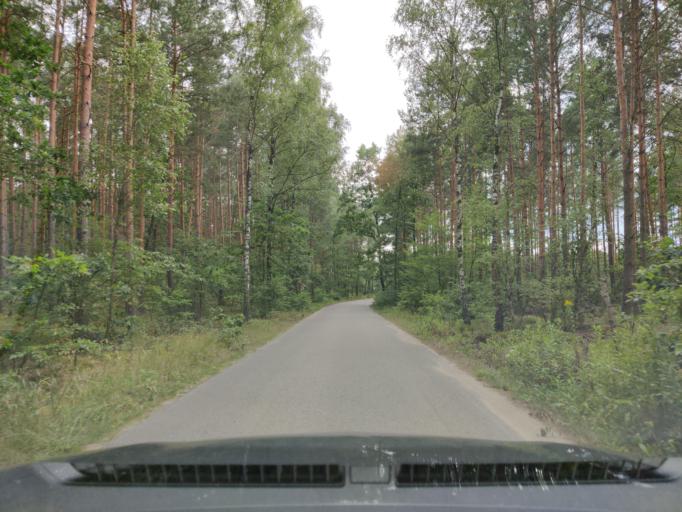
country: PL
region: Masovian Voivodeship
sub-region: Powiat pultuski
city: Pultusk
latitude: 52.7389
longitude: 21.1399
